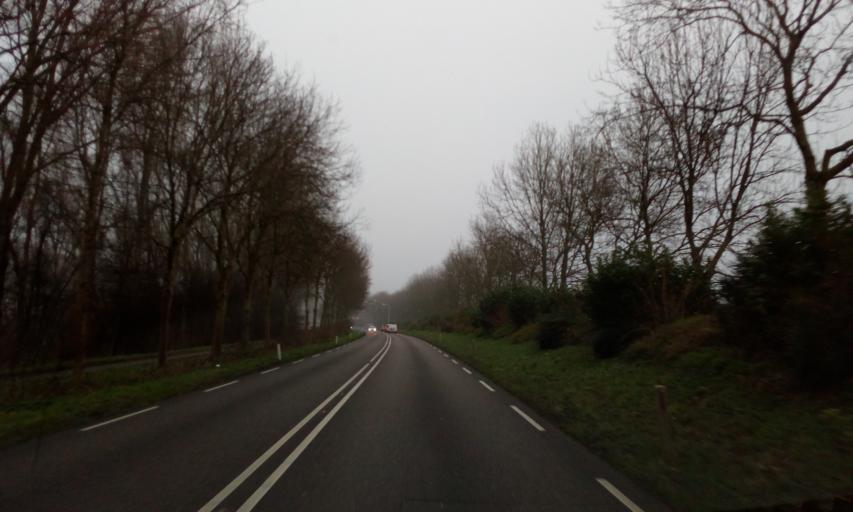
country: NL
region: South Holland
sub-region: Gemeente Capelle aan den IJssel
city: Capelle aan den IJssel
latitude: 51.9760
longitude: 4.6127
